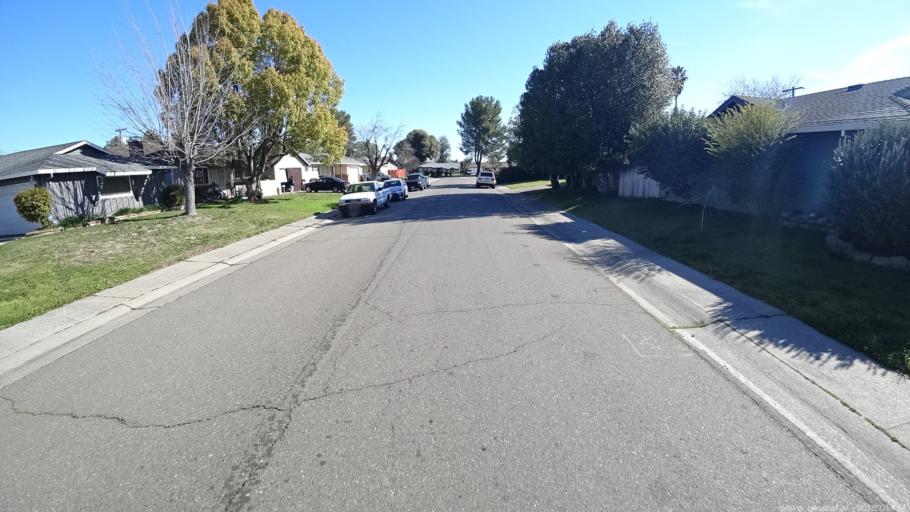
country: US
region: California
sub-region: Sacramento County
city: Parkway
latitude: 38.4877
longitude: -121.4493
